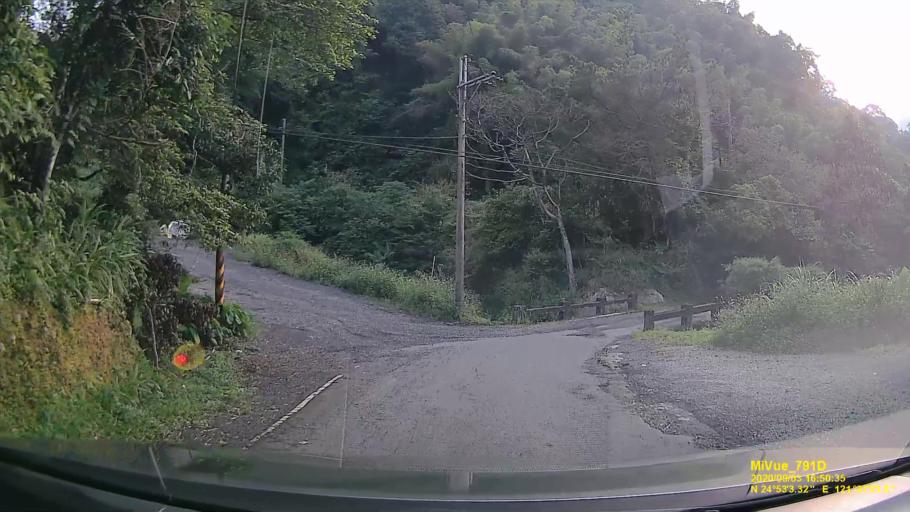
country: TW
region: Taipei
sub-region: Taipei
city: Banqiao
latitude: 24.8843
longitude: 121.4560
